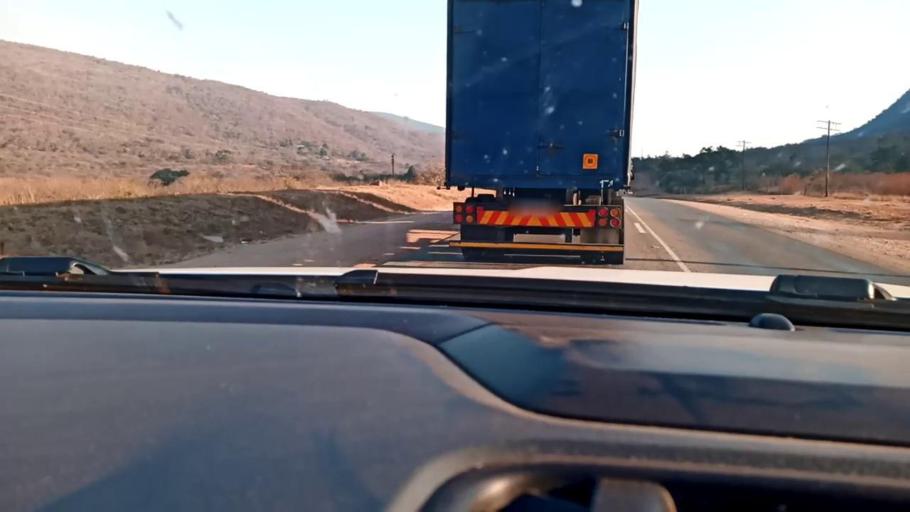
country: ZA
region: Limpopo
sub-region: Mopani District Municipality
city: Duiwelskloof
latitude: -23.6549
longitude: 30.1703
